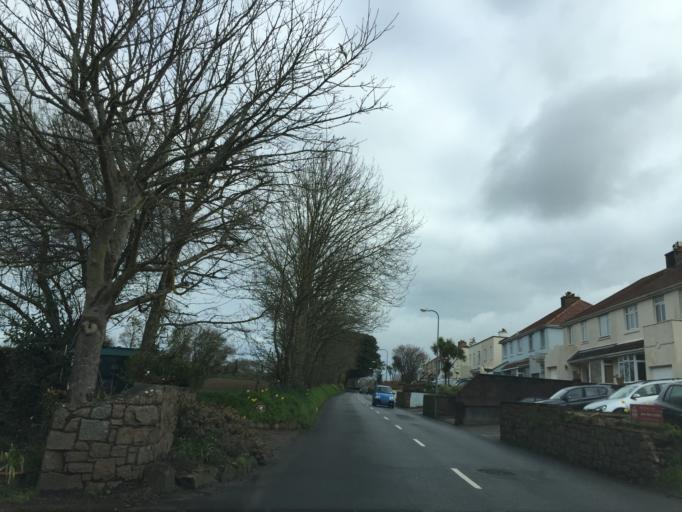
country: JE
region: St Helier
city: Saint Helier
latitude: 49.2088
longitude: -2.1425
